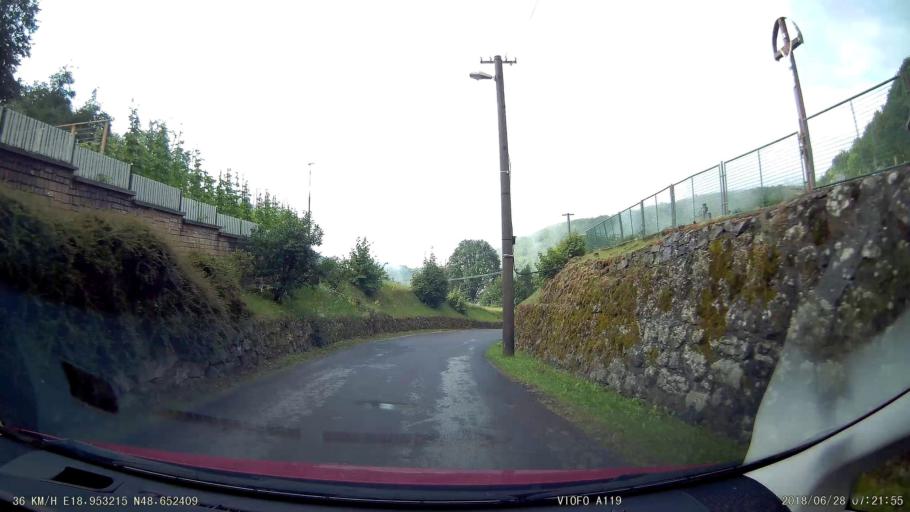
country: SK
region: Banskobystricky
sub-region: Okres Ziar nad Hronom
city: Kremnica
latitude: 48.6522
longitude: 18.9532
